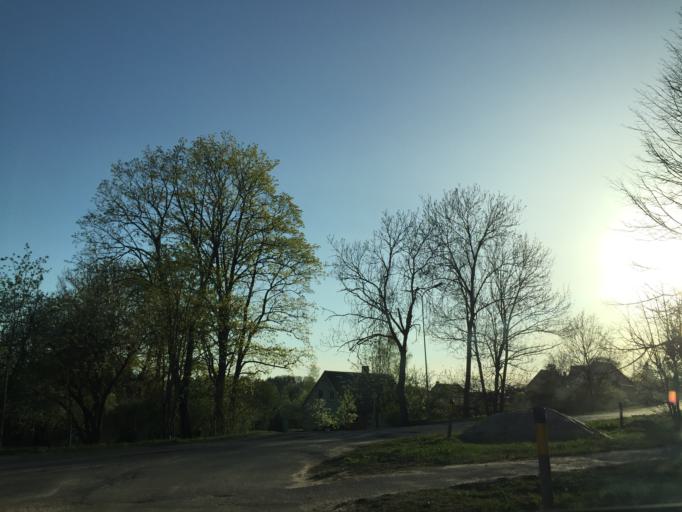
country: LV
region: Koknese
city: Koknese
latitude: 56.7217
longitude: 25.4807
